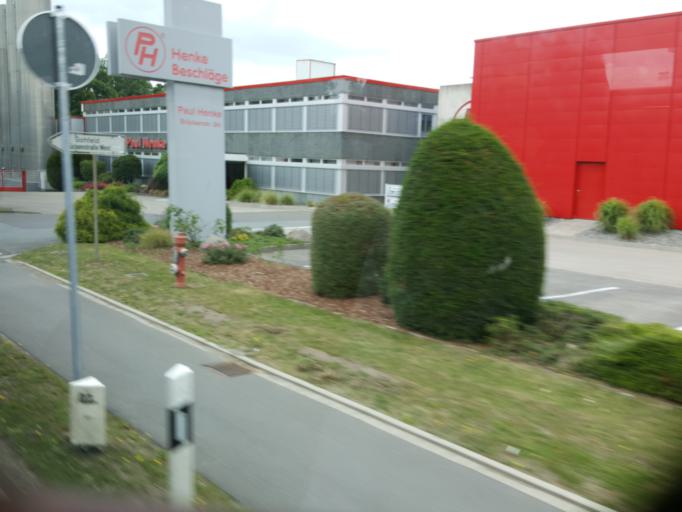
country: DE
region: North Rhine-Westphalia
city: Bad Oeynhausen
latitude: 52.2125
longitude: 8.7600
